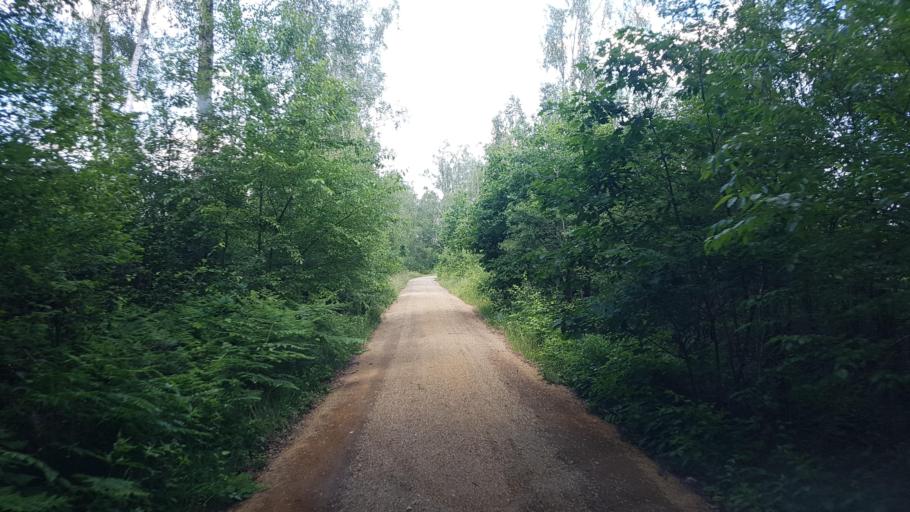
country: DE
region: Brandenburg
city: Plessa
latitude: 51.4956
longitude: 13.6215
